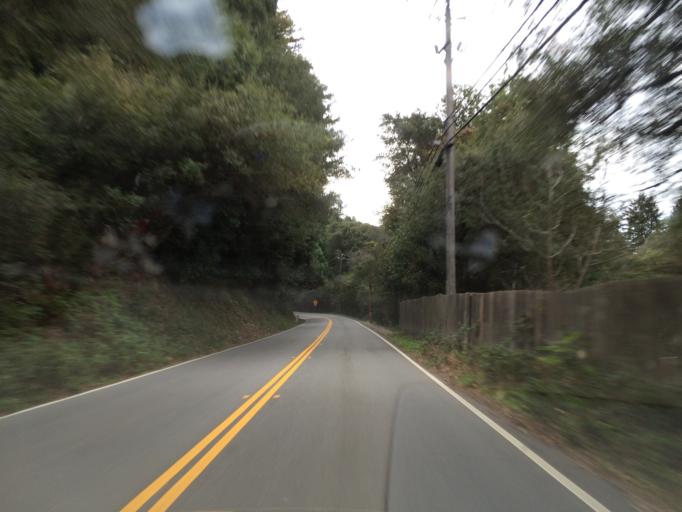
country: US
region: California
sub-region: Santa Cruz County
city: Boulder Creek
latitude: 37.1068
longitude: -122.1429
